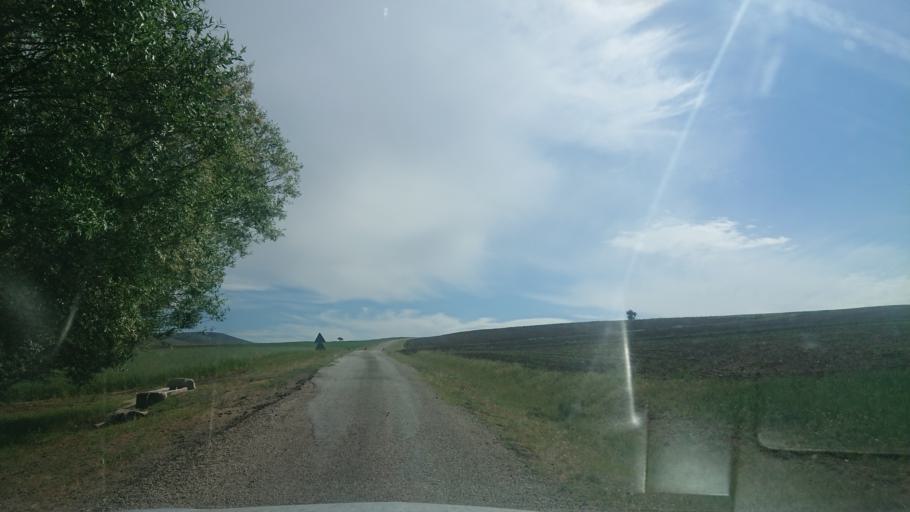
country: TR
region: Aksaray
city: Ortakoy
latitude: 38.8146
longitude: 33.9963
